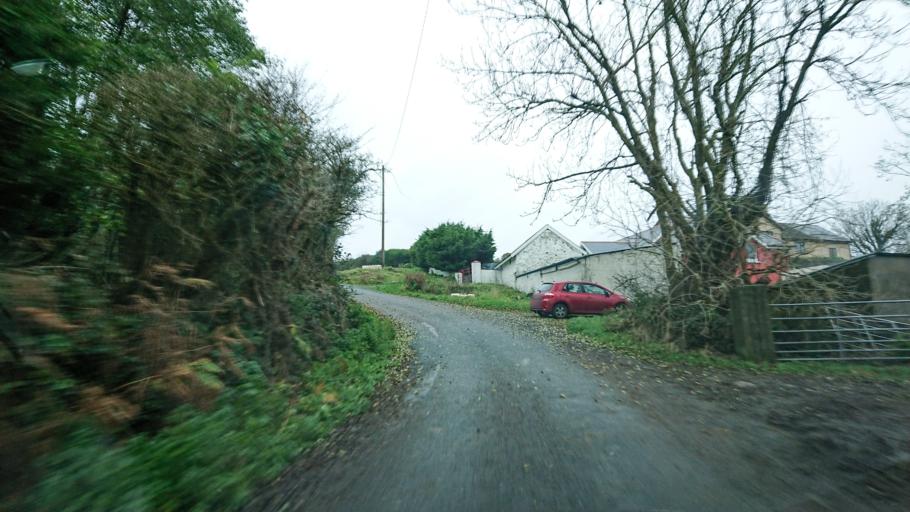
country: IE
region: Munster
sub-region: Waterford
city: Tra Mhor
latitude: 52.2000
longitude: -7.1604
